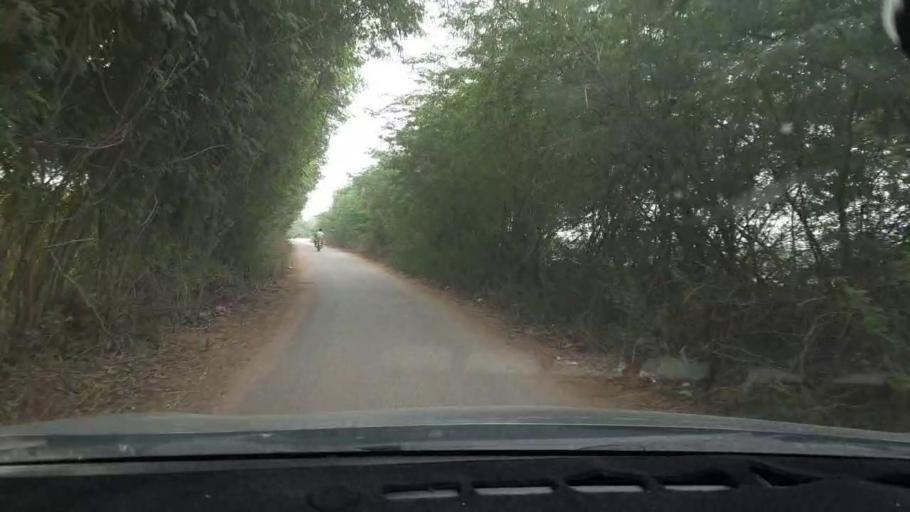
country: PK
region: Sindh
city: Malir Cantonment
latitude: 24.9247
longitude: 67.3206
